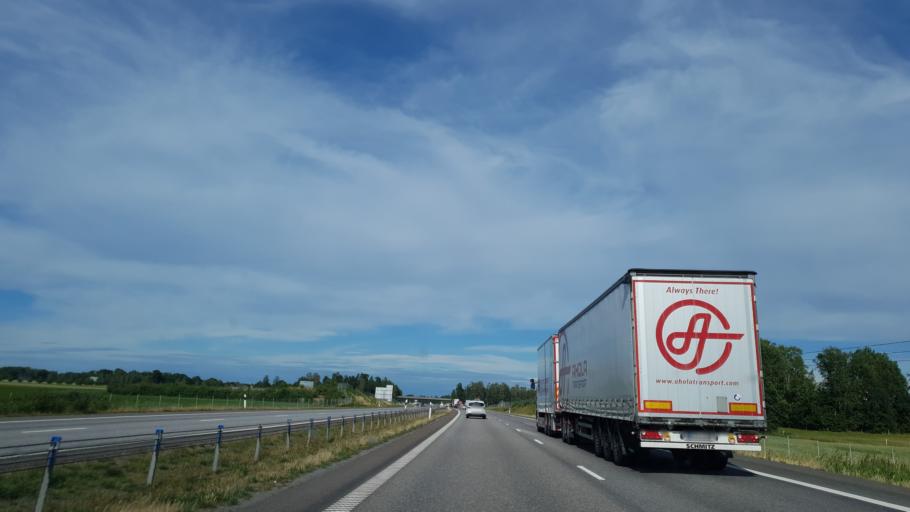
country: SE
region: OEstergoetland
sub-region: Linkopings Kommun
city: Ekangen
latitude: 58.4394
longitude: 15.7045
